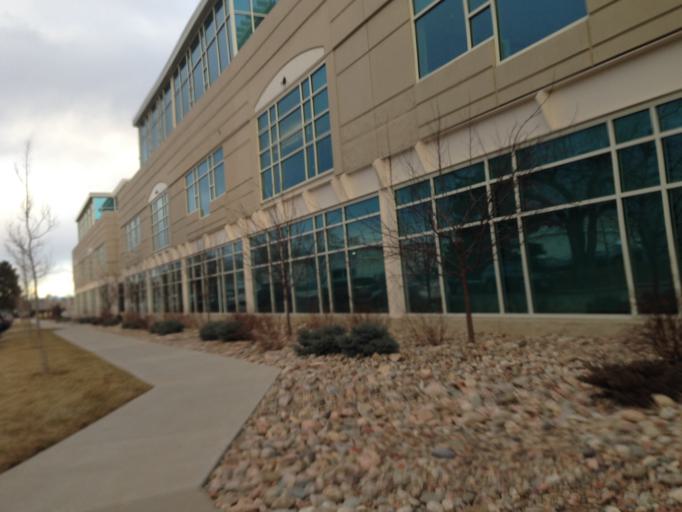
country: US
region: Colorado
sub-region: Boulder County
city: Boulder
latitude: 40.0204
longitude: -105.2495
